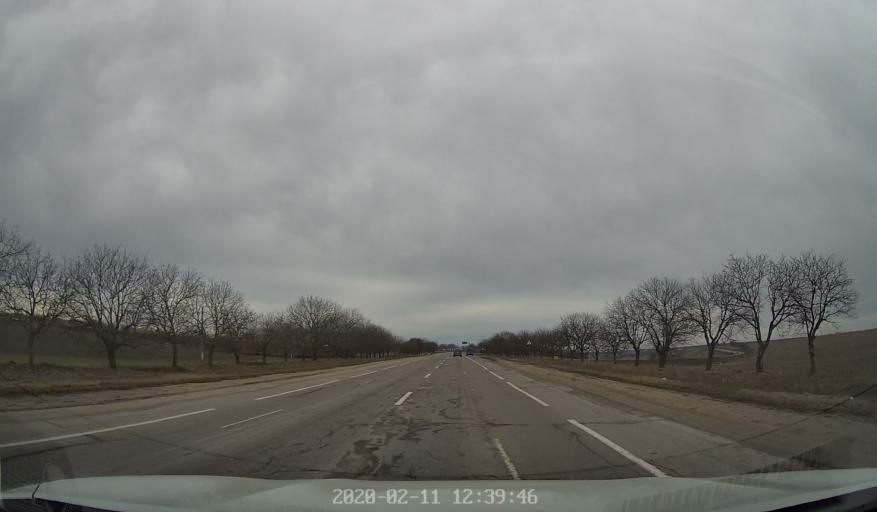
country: MD
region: Raionul Edinet
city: Edinet
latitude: 48.2040
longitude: 27.2667
